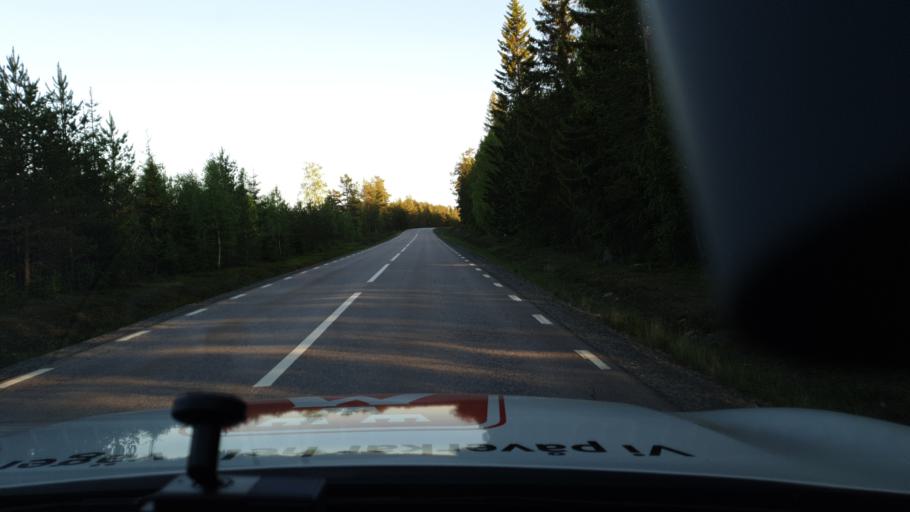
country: SE
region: Vaesterbotten
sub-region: Umea Kommun
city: Ersmark
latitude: 63.8994
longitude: 20.3148
